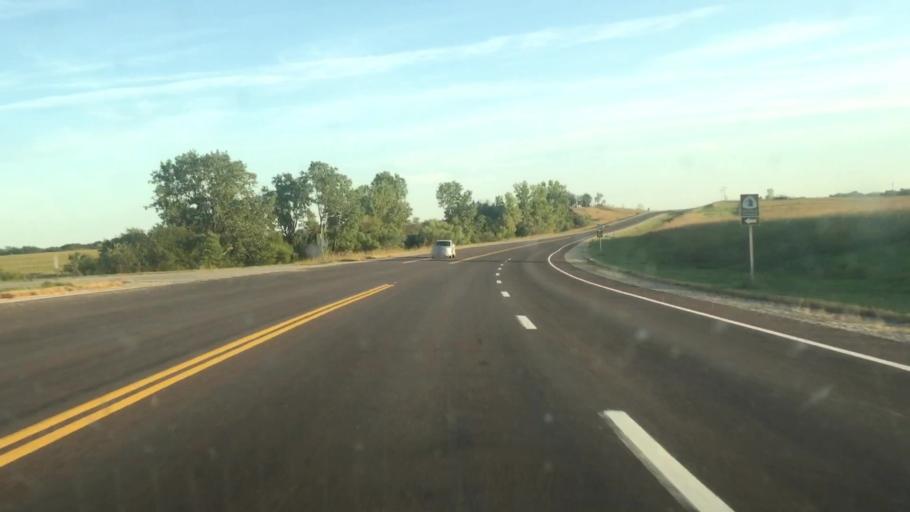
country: US
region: Kansas
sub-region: Atchison County
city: Atchison
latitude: 39.4678
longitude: -95.0951
